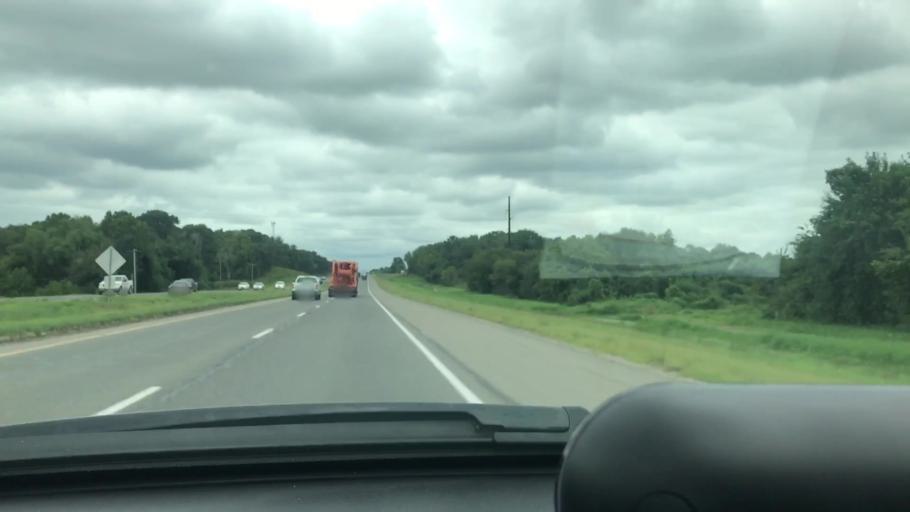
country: US
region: Oklahoma
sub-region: Muskogee County
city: Muskogee
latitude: 35.8183
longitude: -95.4026
